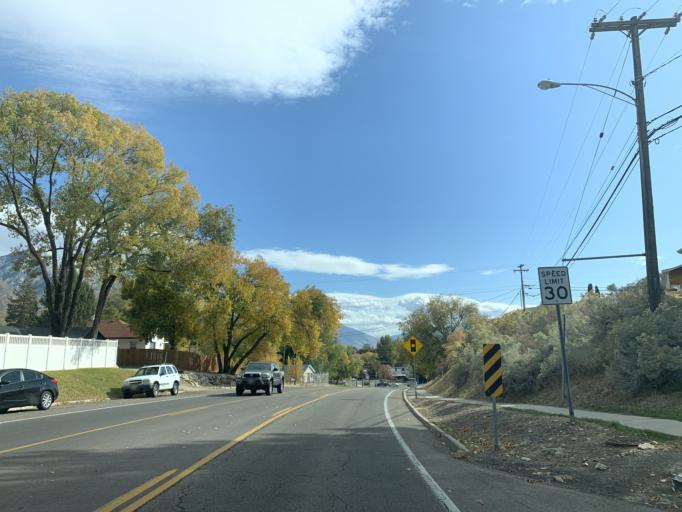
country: US
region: Utah
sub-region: Utah County
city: Provo
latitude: 40.2563
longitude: -111.6751
